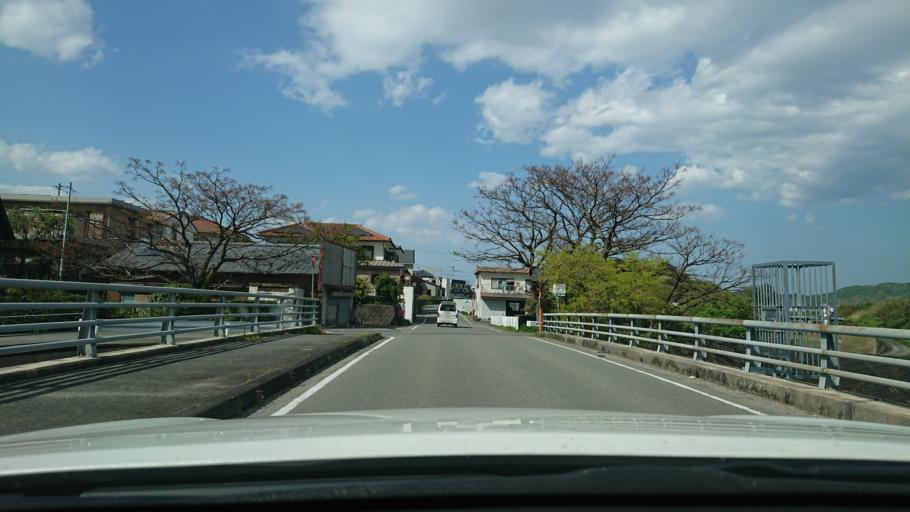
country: JP
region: Tokushima
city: Komatsushimacho
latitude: 34.0006
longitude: 134.5472
